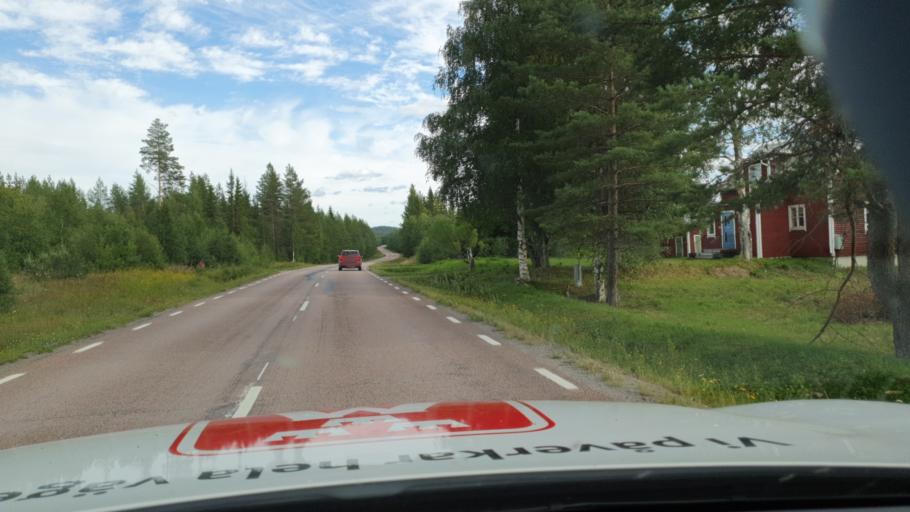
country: SE
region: Jaemtland
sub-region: Stroemsunds Kommun
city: Stroemsund
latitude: 63.6439
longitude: 16.0141
